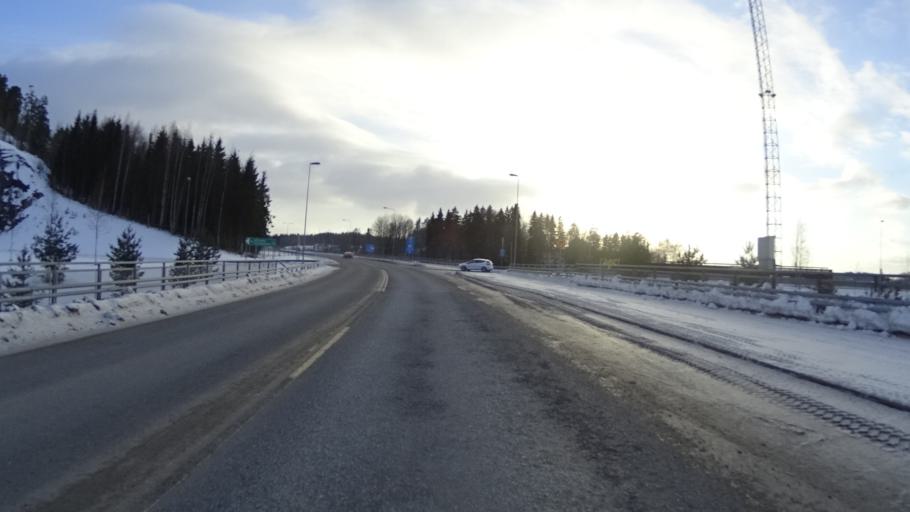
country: FI
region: Uusimaa
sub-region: Helsinki
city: Lohja
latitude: 60.2937
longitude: 24.0665
